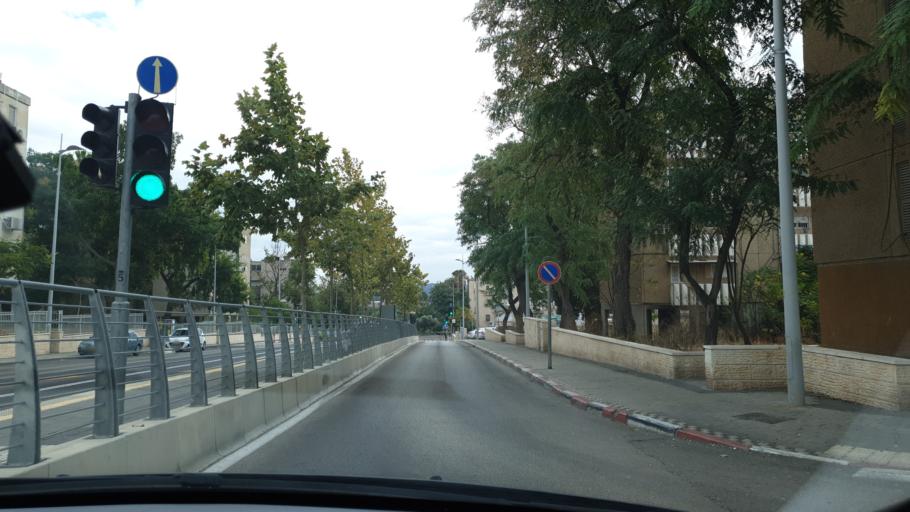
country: IL
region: Haifa
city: Qiryat Ata
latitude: 32.8088
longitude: 35.1162
